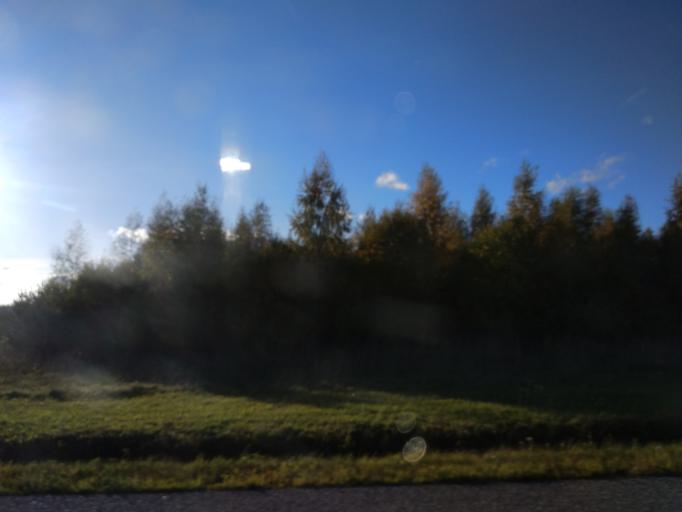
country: EE
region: Polvamaa
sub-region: Polva linn
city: Polva
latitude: 58.0223
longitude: 27.0631
